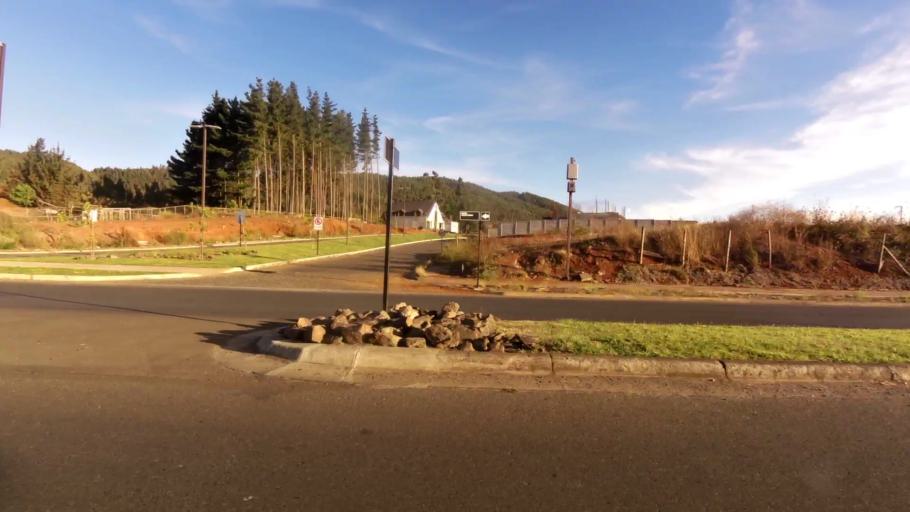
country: CL
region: Biobio
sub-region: Provincia de Concepcion
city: Concepcion
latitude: -36.8639
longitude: -73.0973
